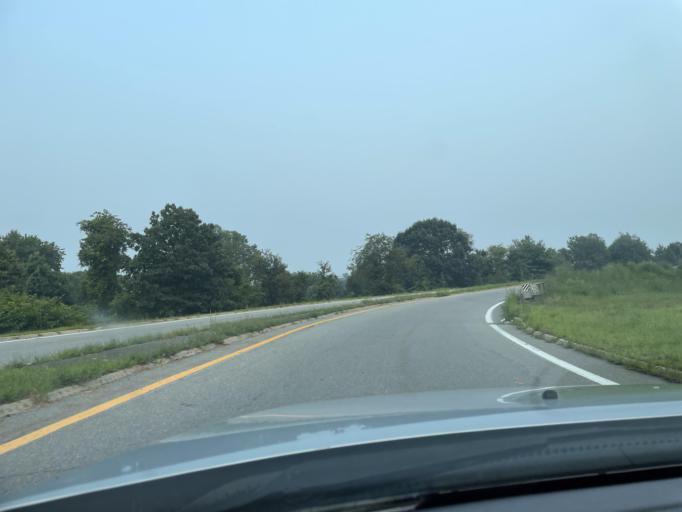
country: US
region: Massachusetts
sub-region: Essex County
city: Lynnfield
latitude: 42.5272
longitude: -71.0650
